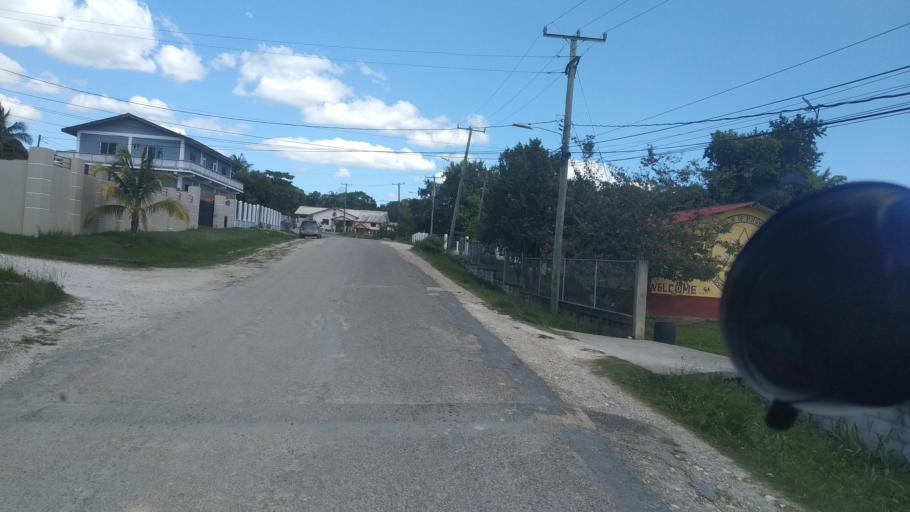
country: BZ
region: Cayo
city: Benque Viejo del Carmen
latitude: 17.0754
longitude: -89.1336
